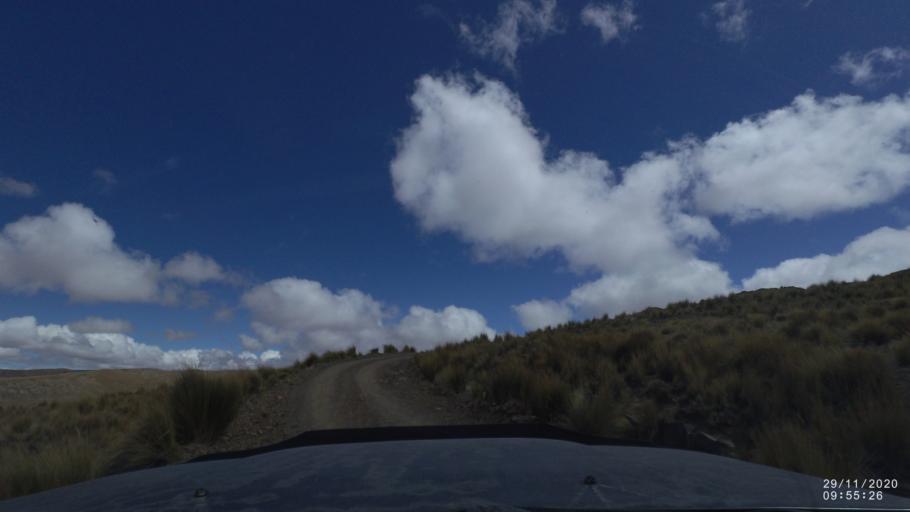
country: BO
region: Cochabamba
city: Cochabamba
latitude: -17.2749
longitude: -66.1786
